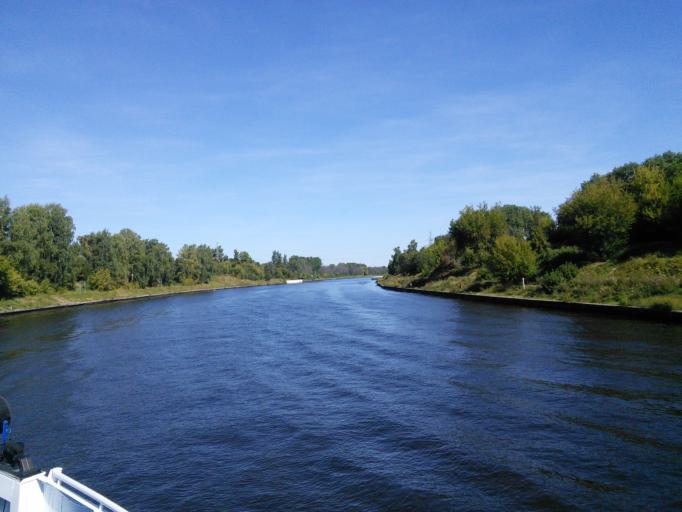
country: RU
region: Moskovskaya
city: Dolgoprudnyy
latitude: 55.9451
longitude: 37.4793
